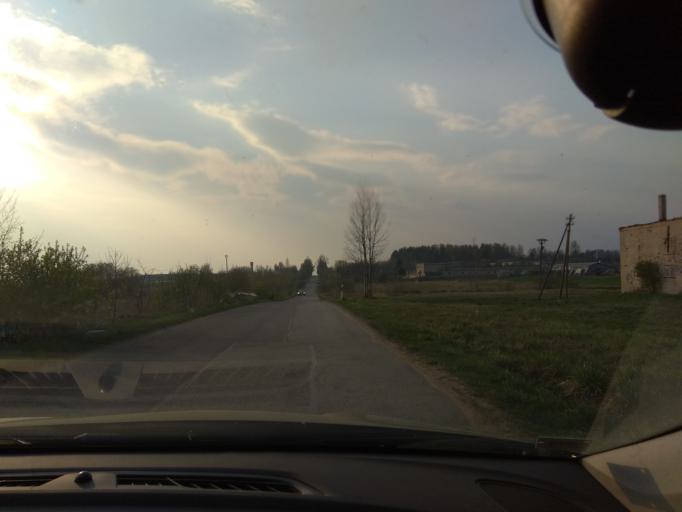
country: LT
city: Baltoji Voke
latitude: 54.5950
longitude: 25.1515
